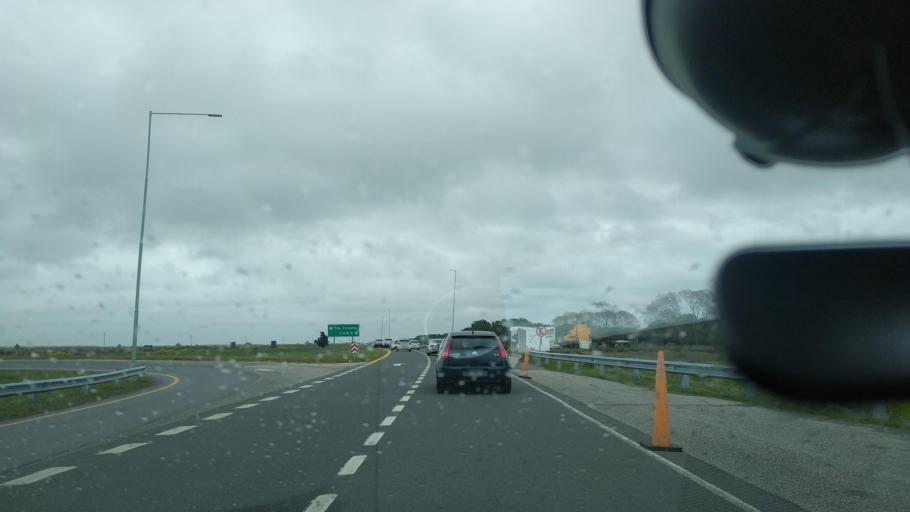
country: AR
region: Buenos Aires
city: San Clemente del Tuyu
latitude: -36.3891
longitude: -56.7424
